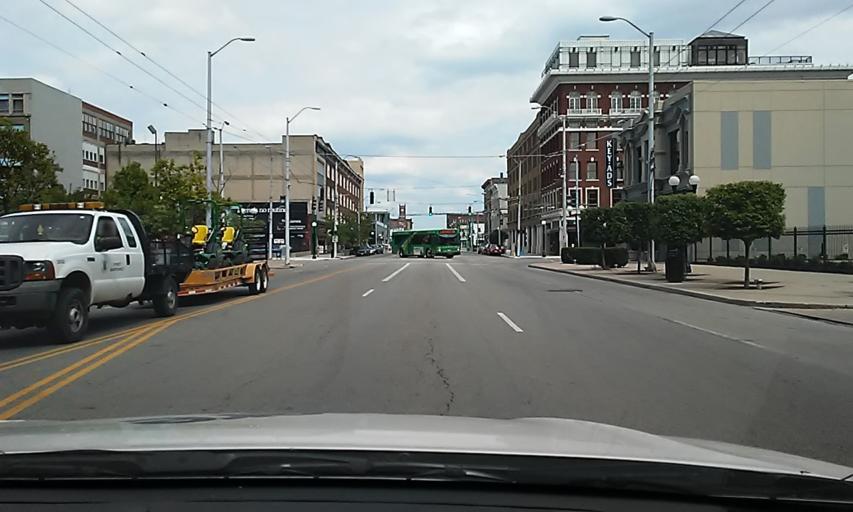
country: US
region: Ohio
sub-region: Montgomery County
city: Dayton
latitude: 39.7597
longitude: -84.1909
